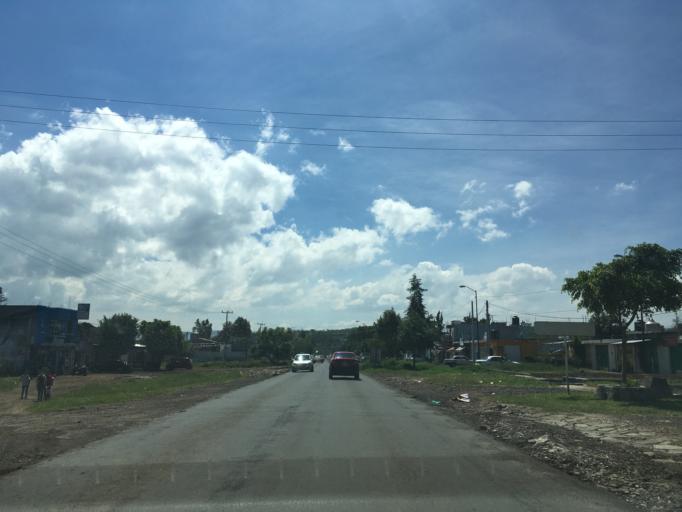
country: MX
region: Michoacan
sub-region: Morelia
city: San Antonio
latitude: 19.6814
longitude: -101.2792
